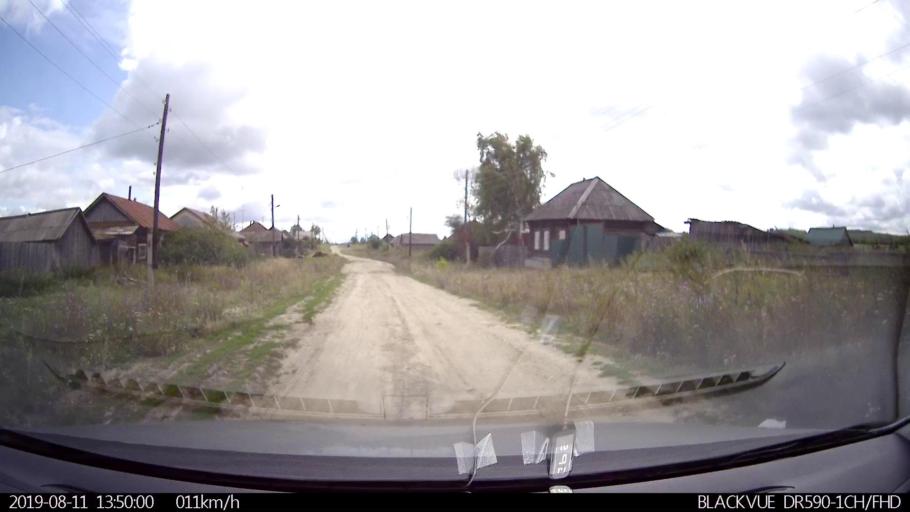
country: RU
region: Ulyanovsk
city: Ignatovka
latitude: 53.8469
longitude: 47.5810
